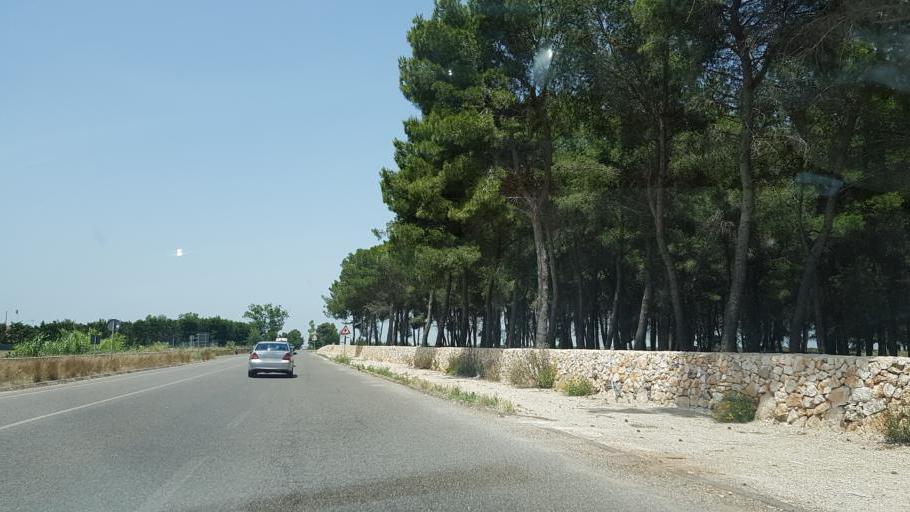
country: IT
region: Apulia
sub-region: Provincia di Lecce
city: Porto Cesareo
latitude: 40.2683
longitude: 17.9099
